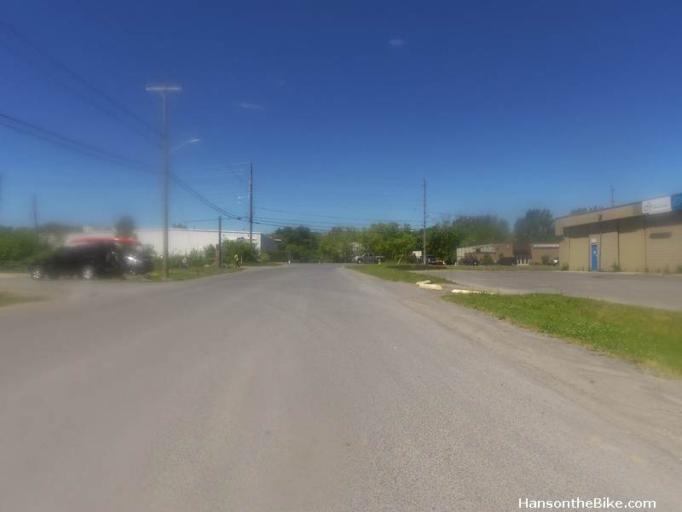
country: CA
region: Ontario
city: Kingston
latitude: 44.2526
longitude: -76.4923
